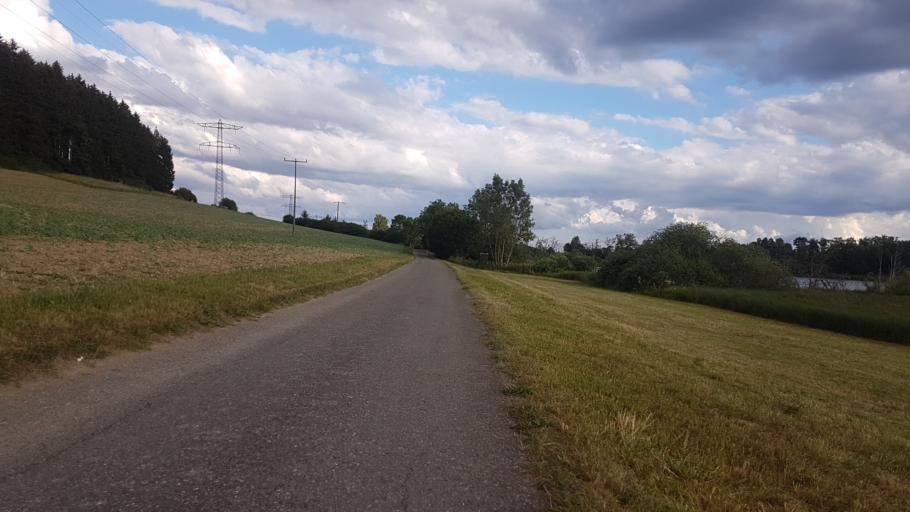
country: DE
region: Baden-Wuerttemberg
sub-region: Freiburg Region
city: Braunlingen
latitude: 47.9868
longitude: 8.4236
